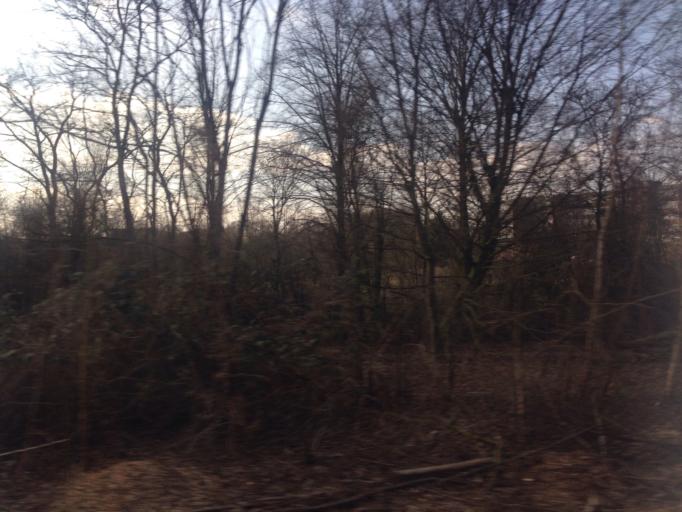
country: DE
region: North Rhine-Westphalia
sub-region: Regierungsbezirk Munster
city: Muenster
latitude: 51.9867
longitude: 7.6377
